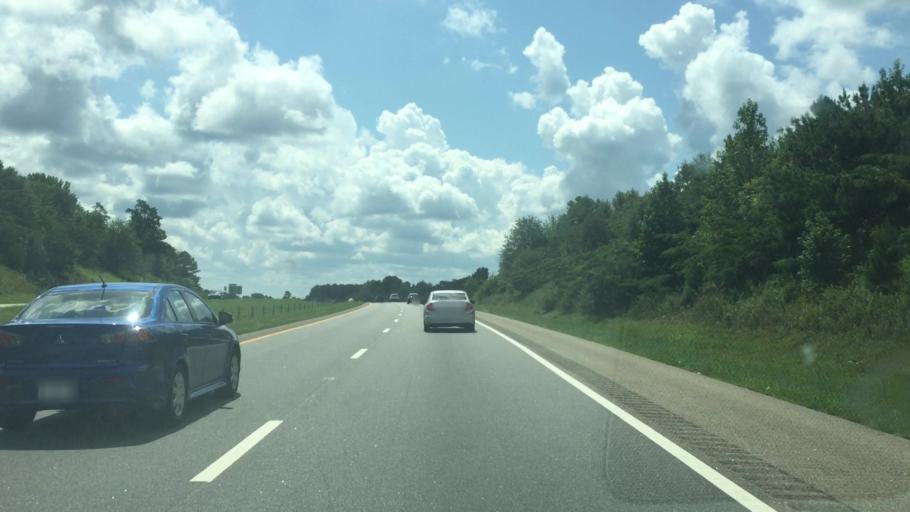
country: US
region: North Carolina
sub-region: Richmond County
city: Cordova
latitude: 34.9375
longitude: -79.8409
